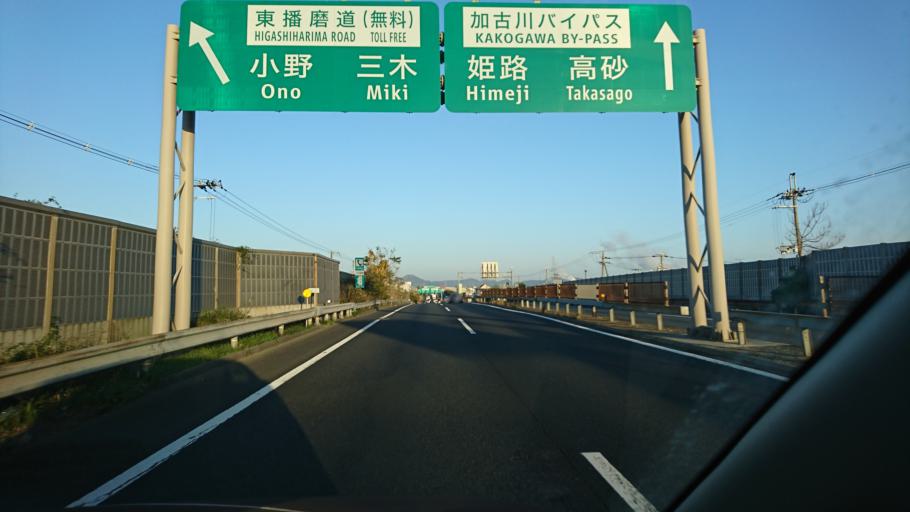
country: JP
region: Hyogo
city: Kakogawacho-honmachi
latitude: 34.7545
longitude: 134.8628
